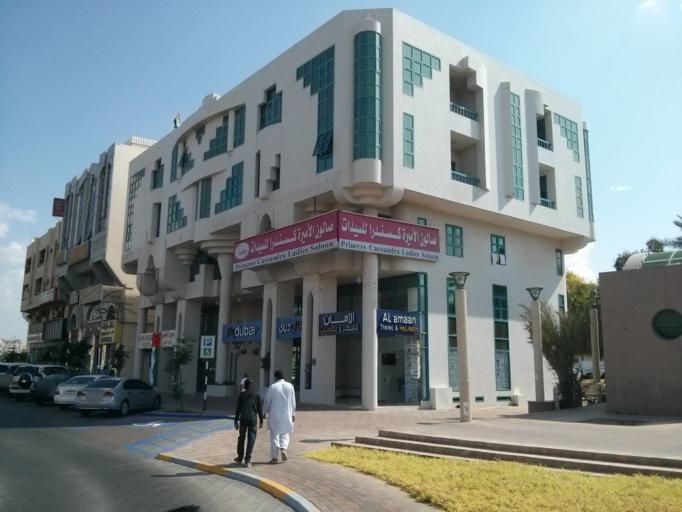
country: AE
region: Abu Dhabi
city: Al Ain
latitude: 24.2223
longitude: 55.7669
